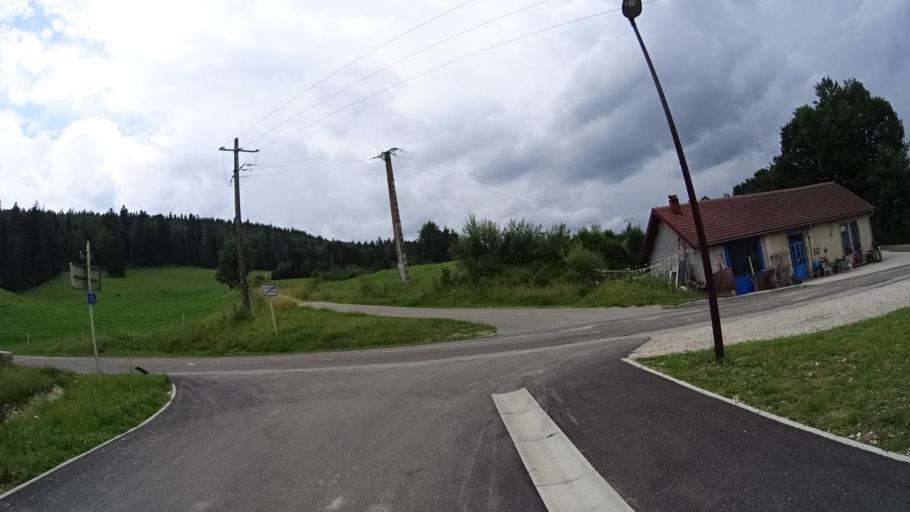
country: FR
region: Franche-Comte
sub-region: Departement du Doubs
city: Les Fourgs
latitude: 46.8177
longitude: 6.3298
